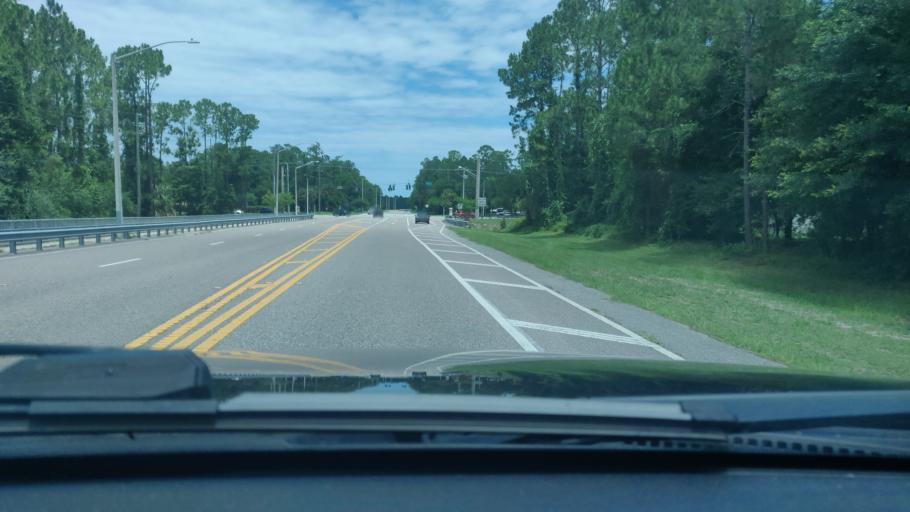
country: US
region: Florida
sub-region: Flagler County
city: Palm Coast
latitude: 29.5516
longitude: -81.2562
